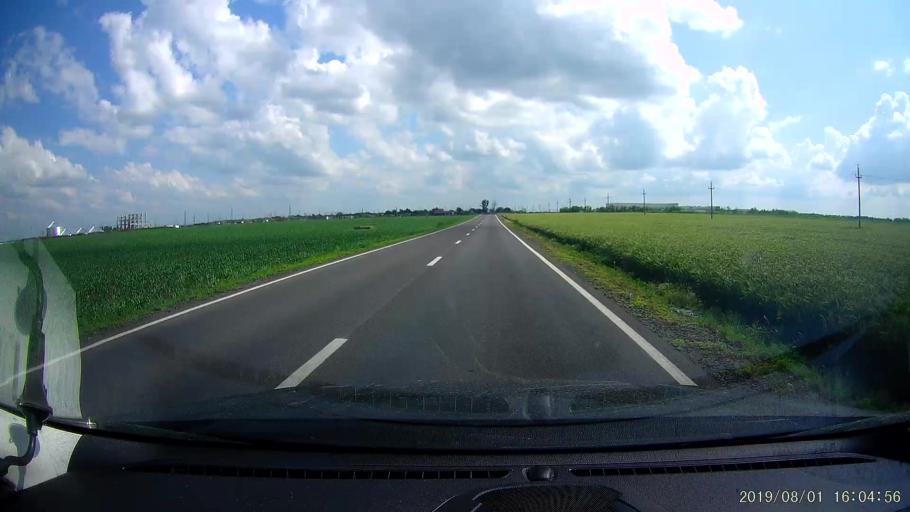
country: RO
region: Calarasi
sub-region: Comuna Dragalina
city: Drajna Noua
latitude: 44.4351
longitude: 27.3780
